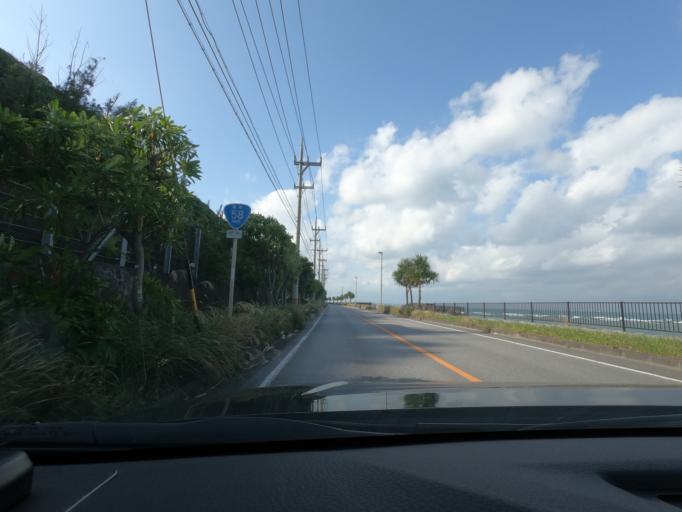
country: JP
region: Okinawa
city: Nago
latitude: 26.7628
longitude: 128.1928
